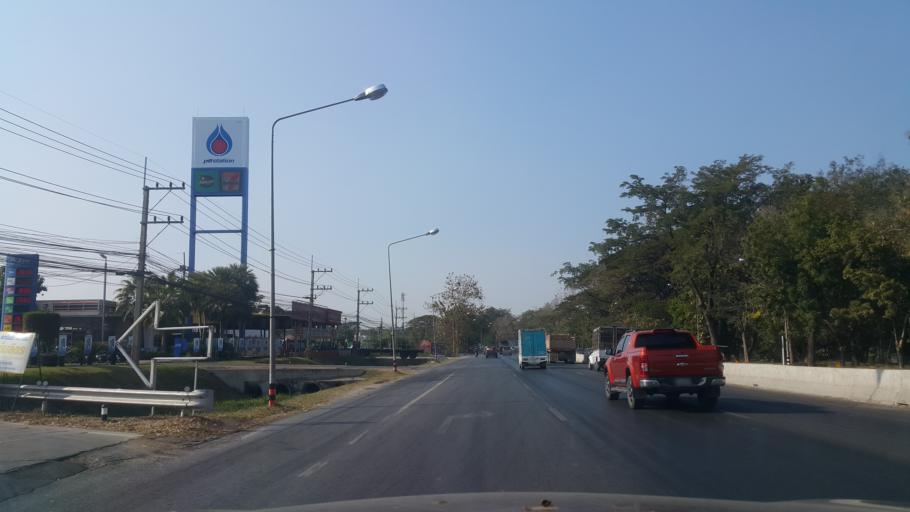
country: TH
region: Nakhon Ratchasima
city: Nakhon Ratchasima
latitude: 14.9153
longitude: 102.0662
